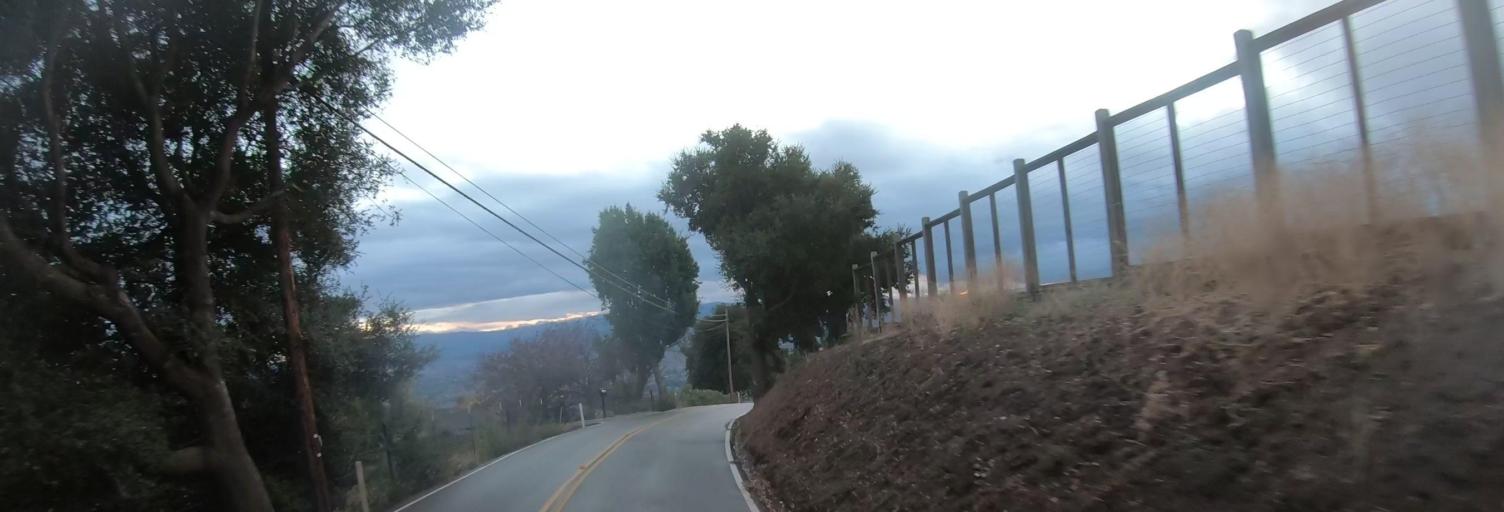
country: US
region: California
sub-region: Santa Clara County
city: East Foothills
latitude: 37.3288
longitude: -121.7462
